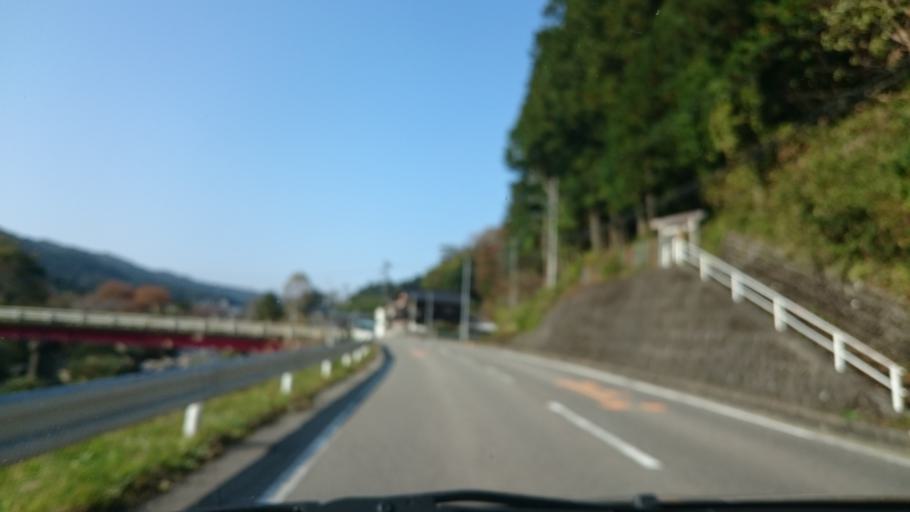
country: JP
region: Gifu
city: Nakatsugawa
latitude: 35.7236
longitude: 137.3557
